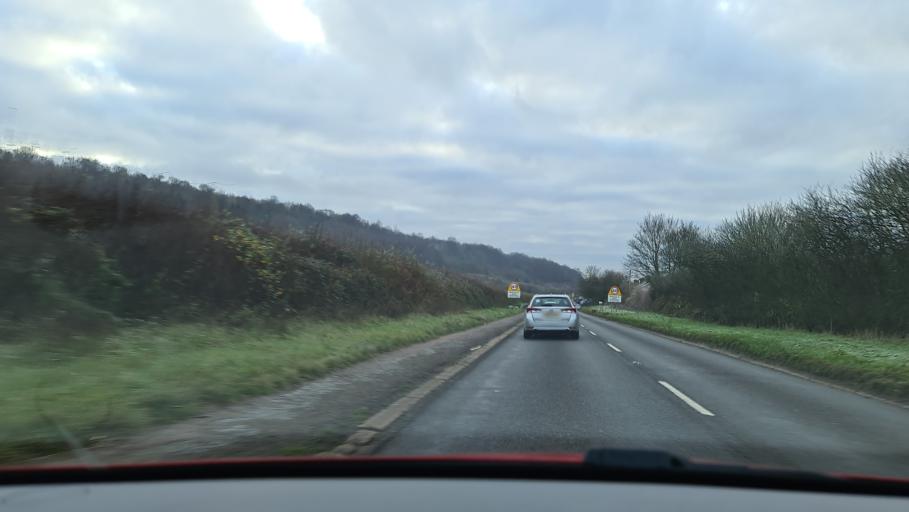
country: GB
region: England
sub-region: Buckinghamshire
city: High Wycombe
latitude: 51.6597
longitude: -0.8046
